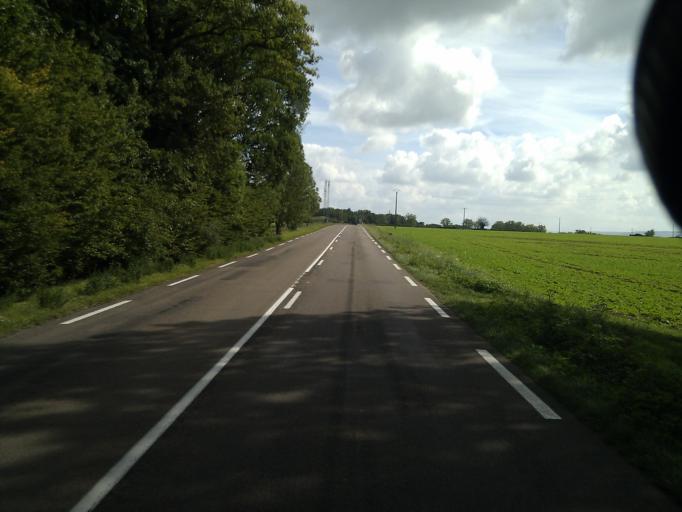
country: FR
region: Bourgogne
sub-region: Departement de la Cote-d'Or
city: Semur-en-Auxois
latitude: 47.4462
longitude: 4.3027
